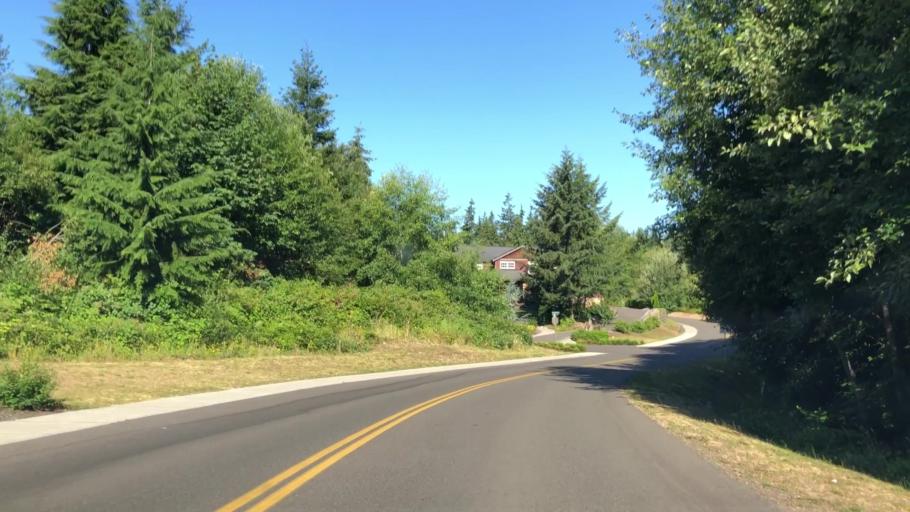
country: US
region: Washington
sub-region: Kitsap County
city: Indianola
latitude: 47.7720
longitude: -122.5197
